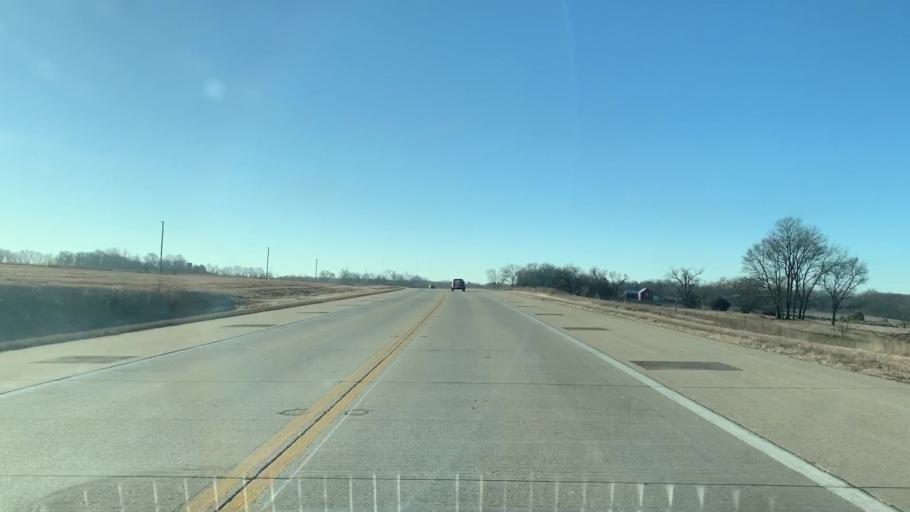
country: US
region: Kansas
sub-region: Crawford County
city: Arma
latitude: 37.5780
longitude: -94.7055
